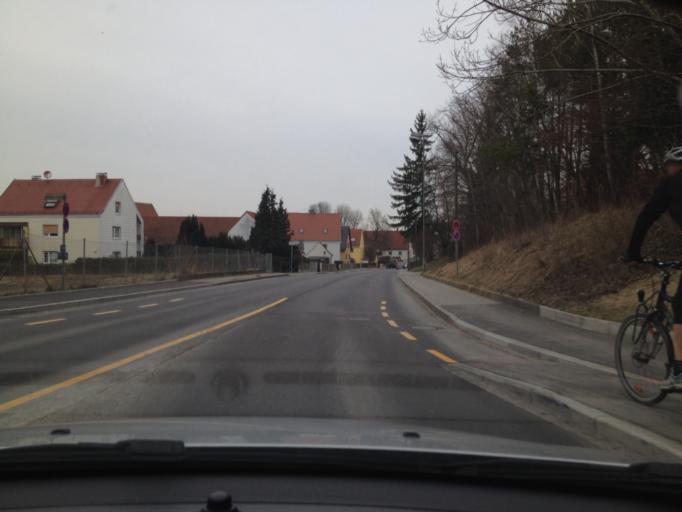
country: DE
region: Bavaria
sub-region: Swabia
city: Bobingen
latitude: 48.3102
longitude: 10.8550
